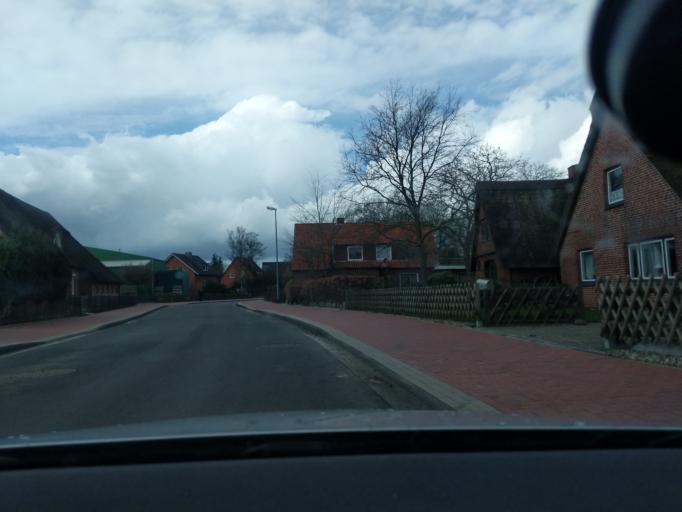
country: DE
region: Lower Saxony
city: Stade
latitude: 53.6151
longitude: 9.4707
